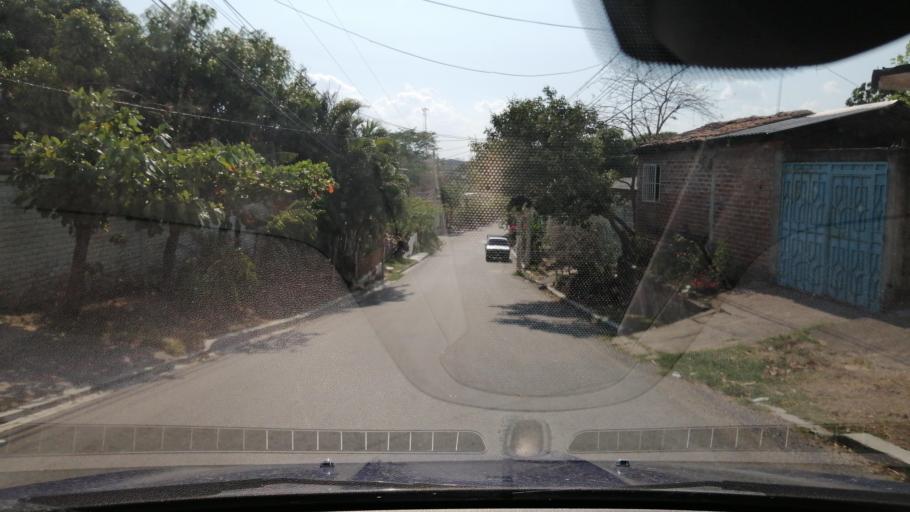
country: SV
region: Santa Ana
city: Metapan
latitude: 14.3297
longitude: -89.4336
